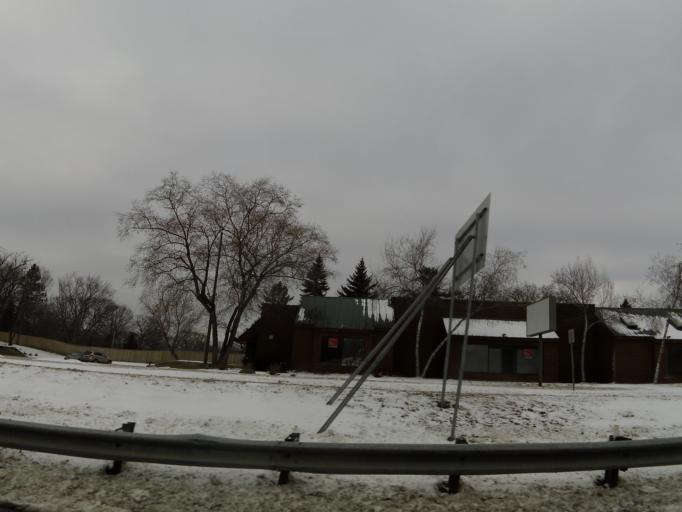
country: US
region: Minnesota
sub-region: Hennepin County
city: Hopkins
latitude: 44.9218
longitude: -93.4698
